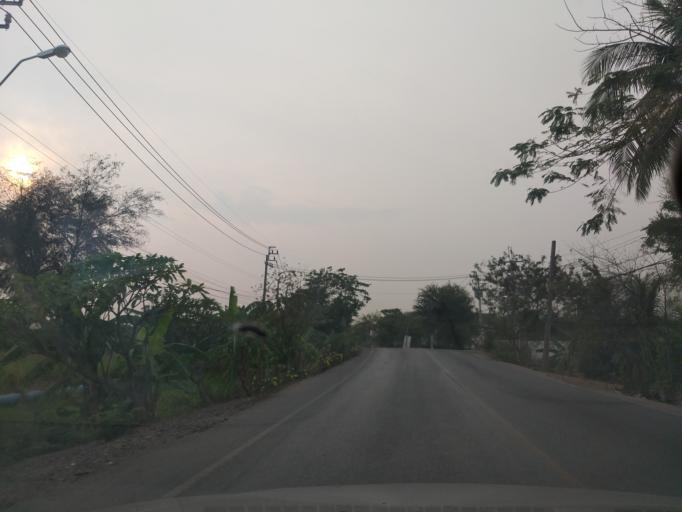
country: TH
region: Bangkok
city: Nong Chok
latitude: 13.8231
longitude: 100.9241
